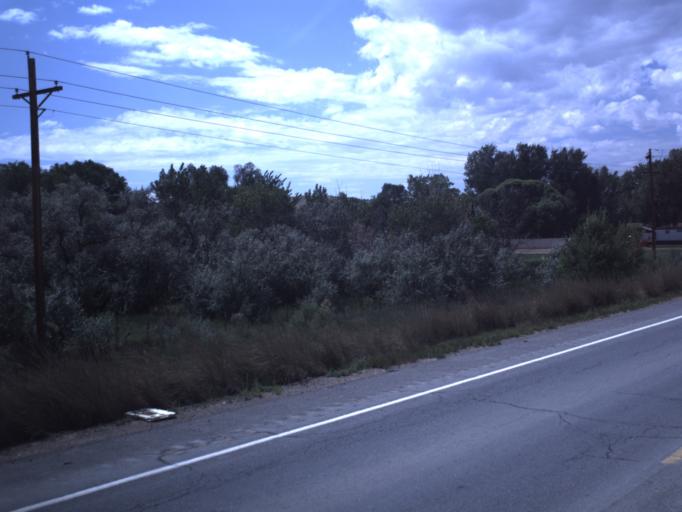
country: US
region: Utah
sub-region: Duchesne County
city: Duchesne
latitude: 40.1616
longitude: -110.3900
